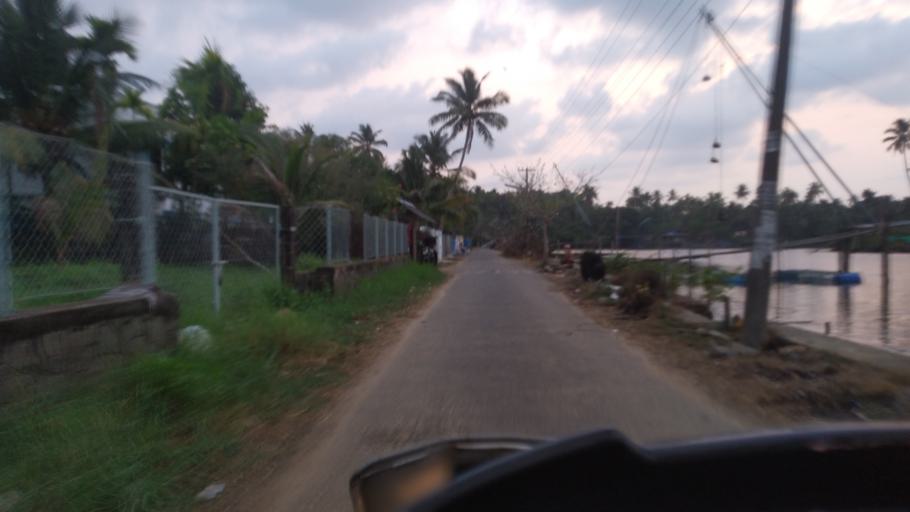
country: IN
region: Kerala
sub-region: Thrissur District
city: Kodungallur
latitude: 10.1424
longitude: 76.2025
